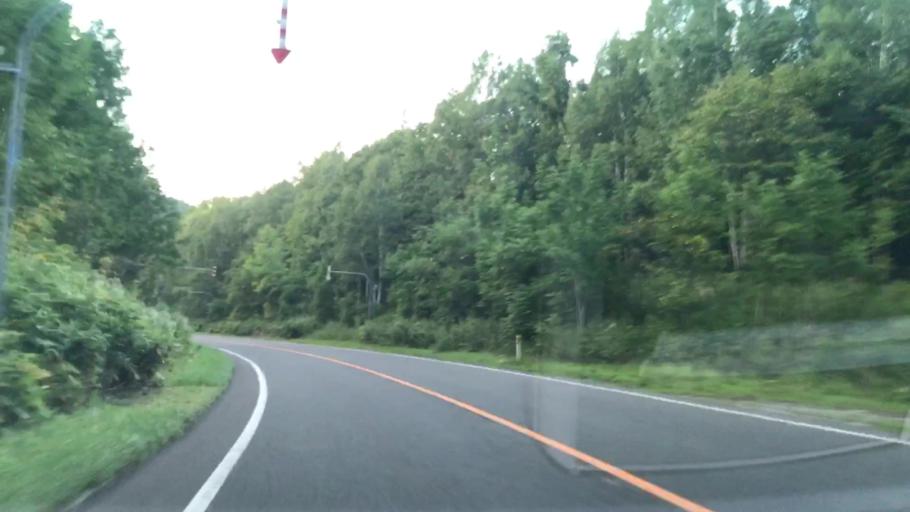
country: JP
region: Hokkaido
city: Sapporo
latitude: 42.9058
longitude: 141.1218
